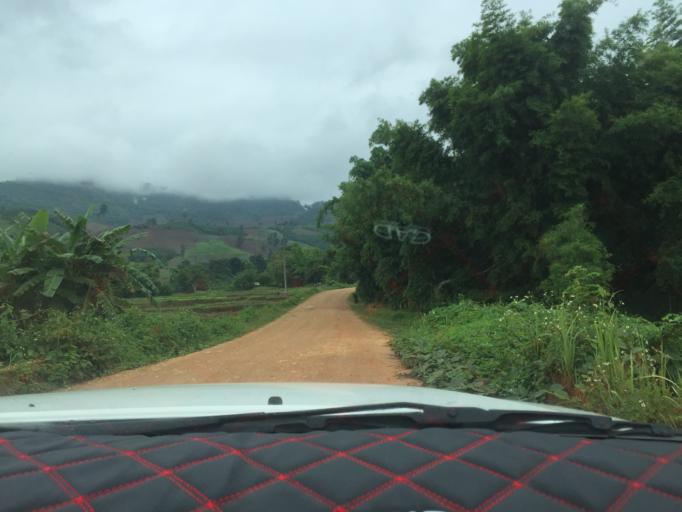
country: TH
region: Phayao
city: Phu Sang
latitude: 19.6779
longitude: 100.5056
